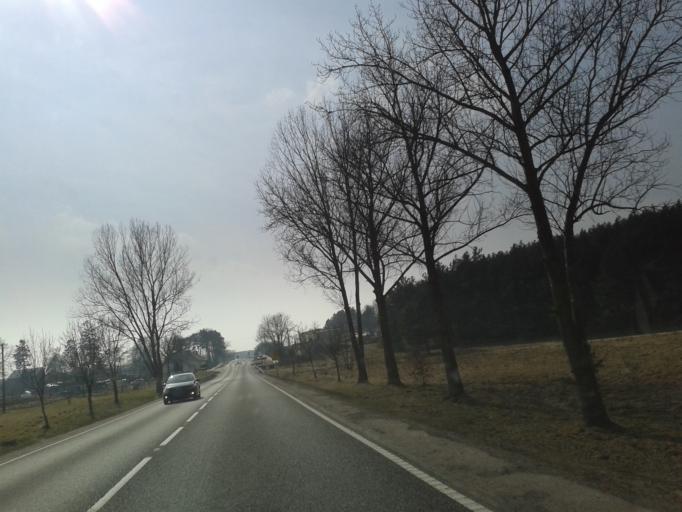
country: PL
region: Pomeranian Voivodeship
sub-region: Powiat czluchowski
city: Debrzno
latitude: 53.5857
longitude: 17.1162
